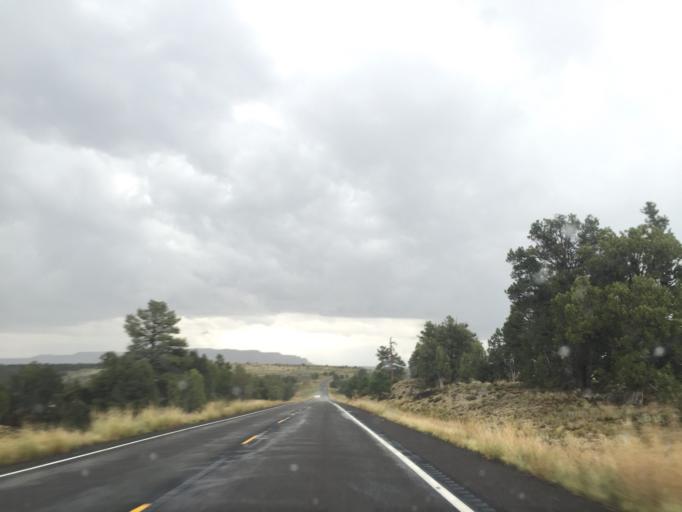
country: US
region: Utah
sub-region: Kane County
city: Kanab
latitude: 37.2352
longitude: -112.7409
